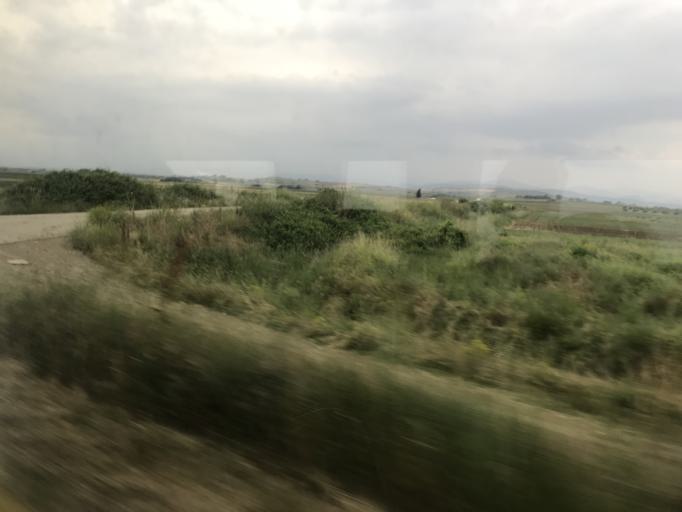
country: GR
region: East Macedonia and Thrace
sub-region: Nomos Rodopis
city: Aratos
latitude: 41.0828
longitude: 25.5454
